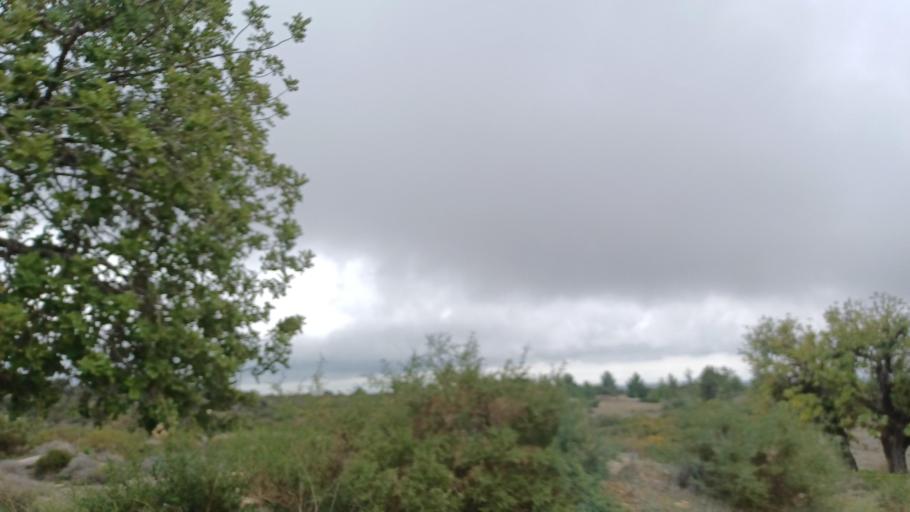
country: CY
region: Limassol
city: Pachna
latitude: 34.7674
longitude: 32.8280
